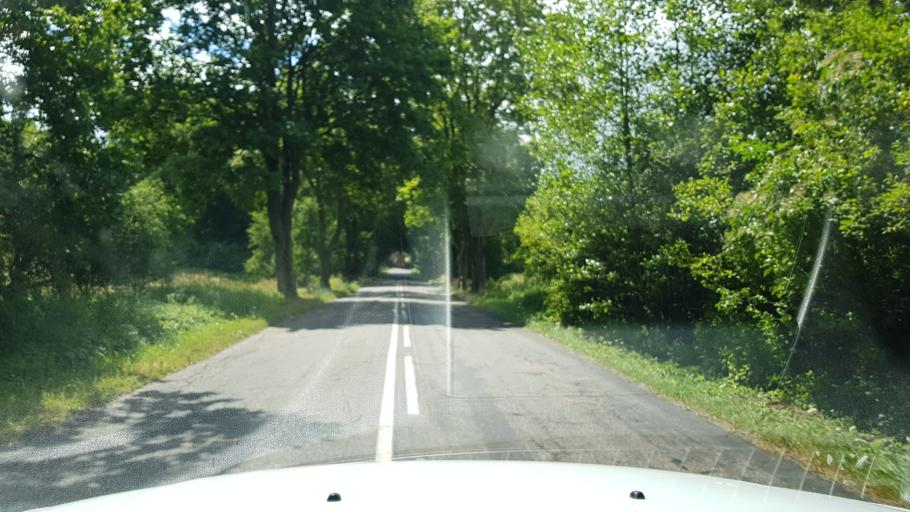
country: PL
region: West Pomeranian Voivodeship
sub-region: Powiat choszczenski
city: Recz
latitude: 53.3395
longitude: 15.5842
